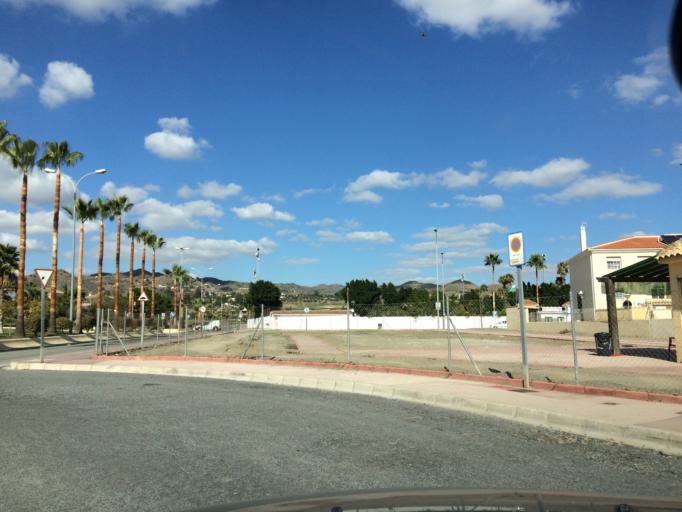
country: ES
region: Andalusia
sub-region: Provincia de Malaga
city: Estacion de Cartama
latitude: 36.7384
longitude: -4.6145
